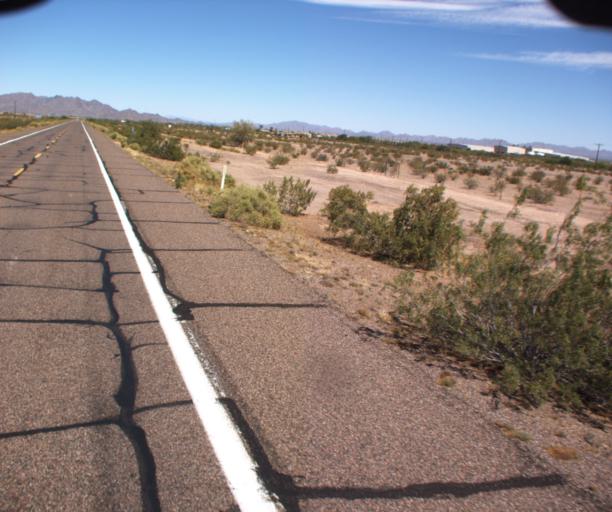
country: US
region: Arizona
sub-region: Maricopa County
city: Gila Bend
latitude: 32.9174
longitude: -112.7351
